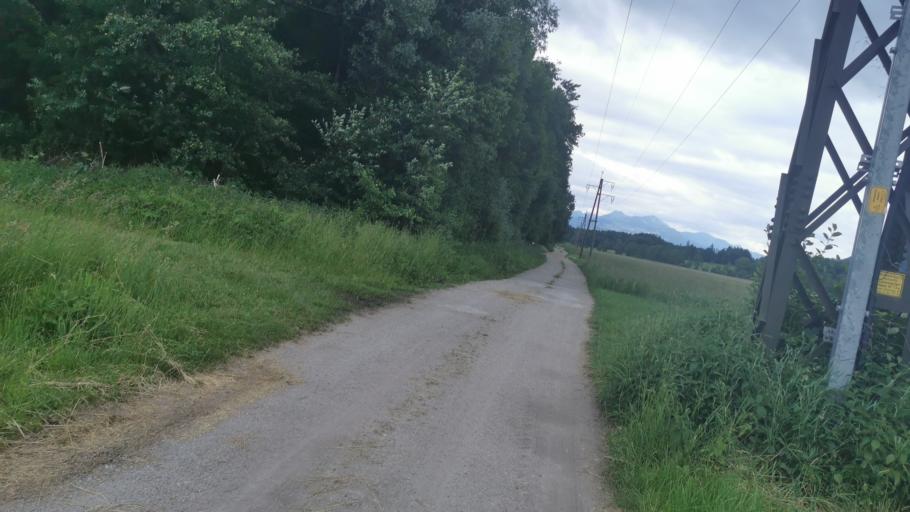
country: DE
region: Bavaria
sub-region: Upper Bavaria
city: Ainring
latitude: 47.7687
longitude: 12.9733
